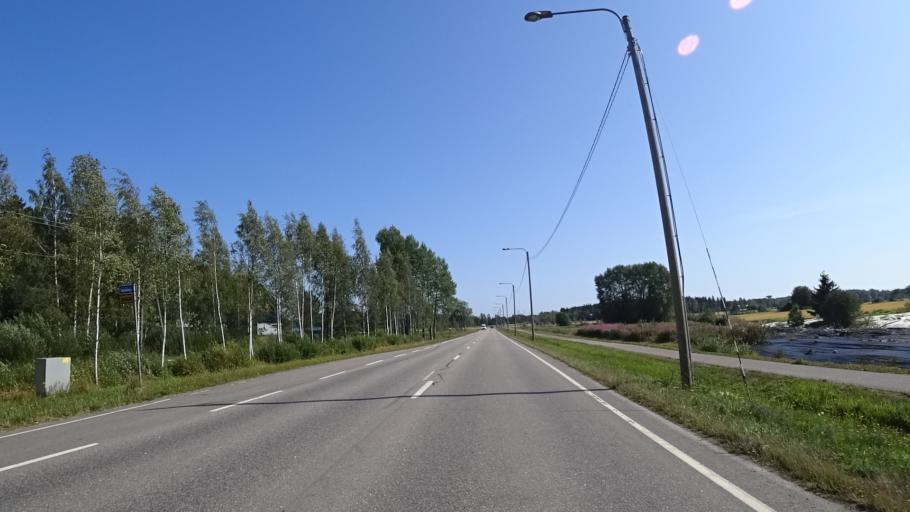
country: FI
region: Kymenlaakso
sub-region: Kotka-Hamina
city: Karhula
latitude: 60.5418
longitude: 26.9265
